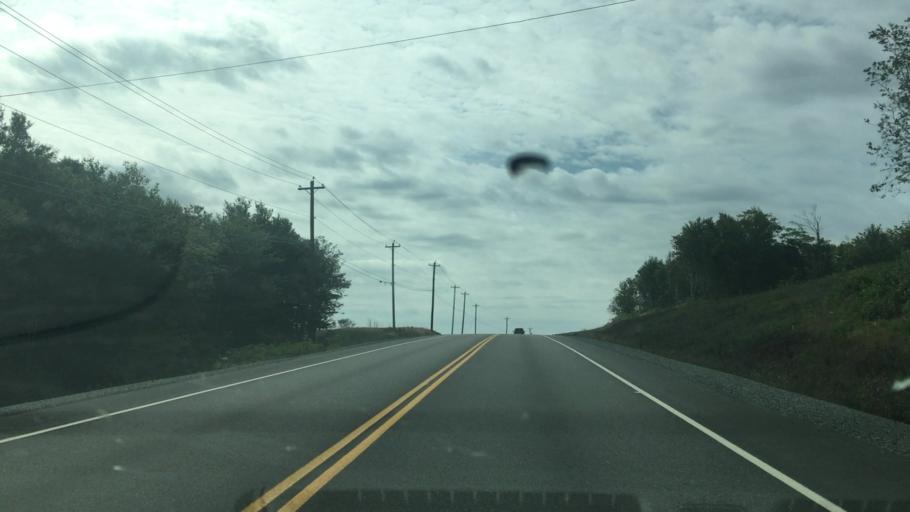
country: CA
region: Nova Scotia
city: Princeville
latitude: 45.6631
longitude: -60.8135
